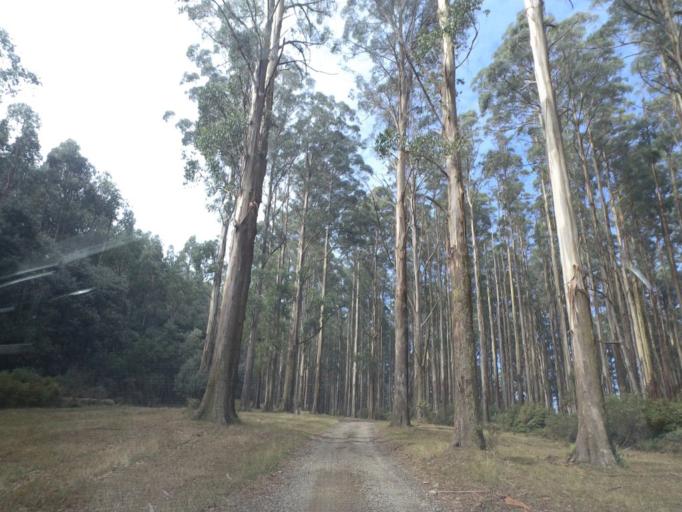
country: AU
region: Victoria
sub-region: Yarra Ranges
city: Healesville
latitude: -37.5853
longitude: 145.5543
